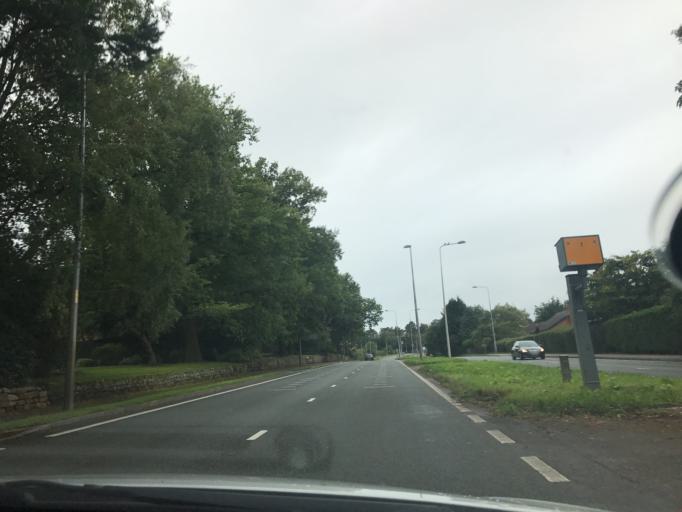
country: GB
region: England
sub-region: Cheshire West and Chester
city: Cuddington
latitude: 53.2331
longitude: -2.5853
